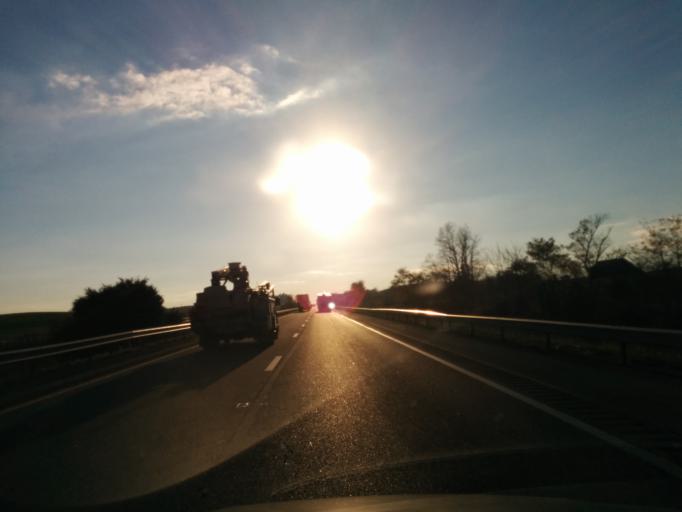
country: US
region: Virginia
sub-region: Rockbridge County
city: East Lexington
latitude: 37.8807
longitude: -79.2970
